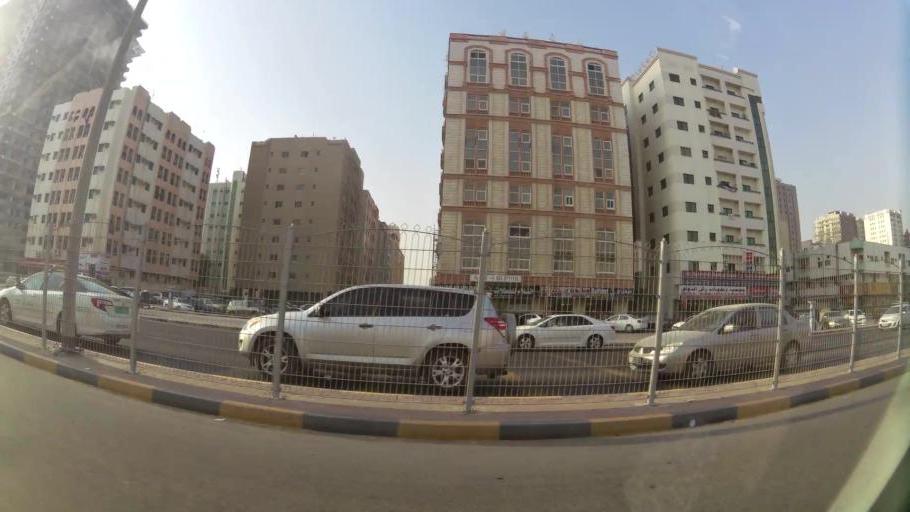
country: AE
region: Ajman
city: Ajman
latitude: 25.3863
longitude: 55.4552
